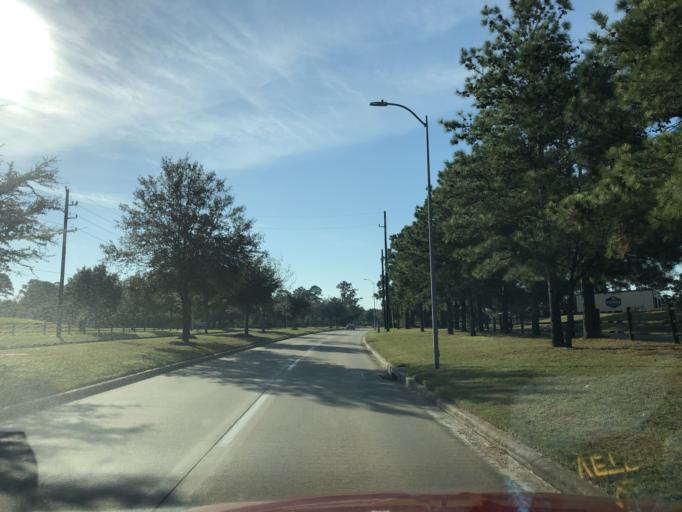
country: US
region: Texas
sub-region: Harris County
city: Tomball
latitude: 30.0462
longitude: -95.5633
